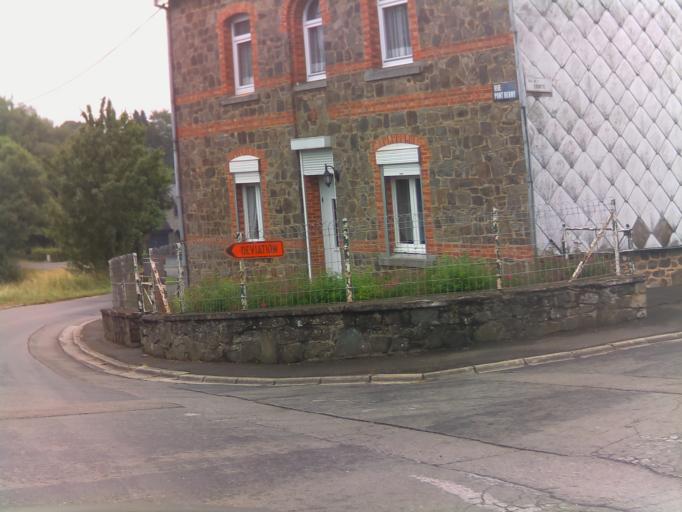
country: BE
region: Wallonia
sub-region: Province du Luxembourg
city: Libin
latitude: 49.9226
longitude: 5.2800
